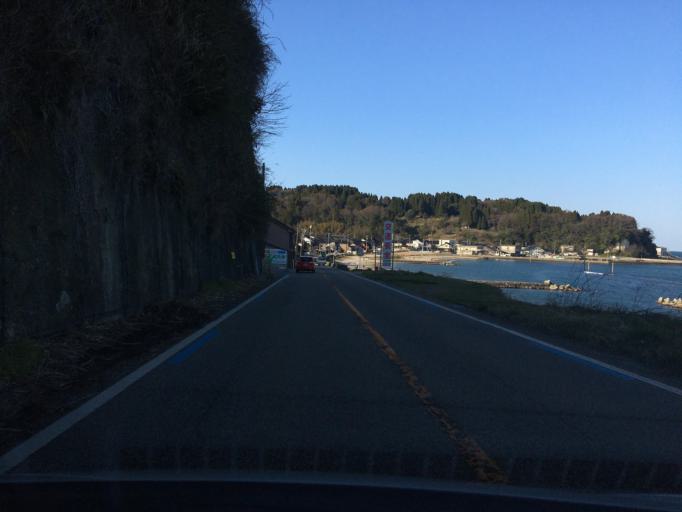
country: JP
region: Toyama
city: Himi
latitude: 36.9088
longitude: 137.0167
